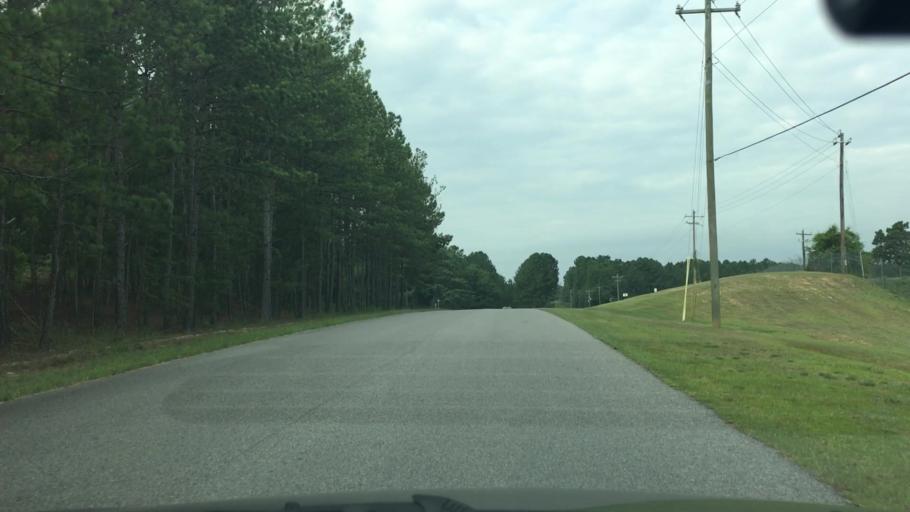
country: US
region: South Carolina
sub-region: Aiken County
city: Aiken
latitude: 33.6519
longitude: -81.6973
